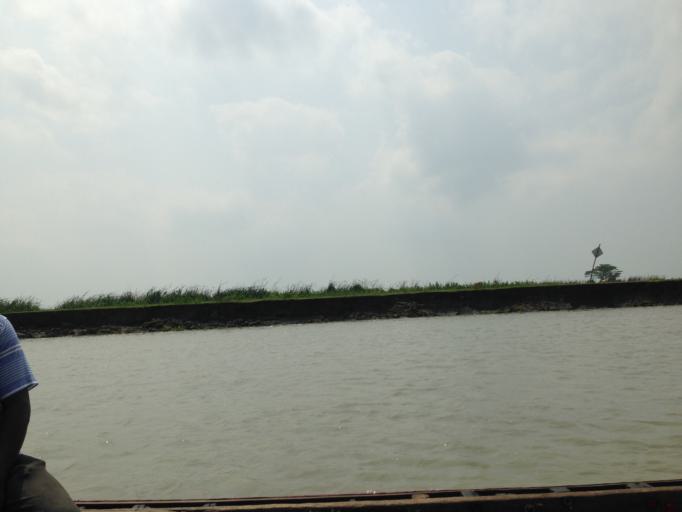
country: BD
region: Chittagong
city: Lakshmipur
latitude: 22.8540
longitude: 90.7585
